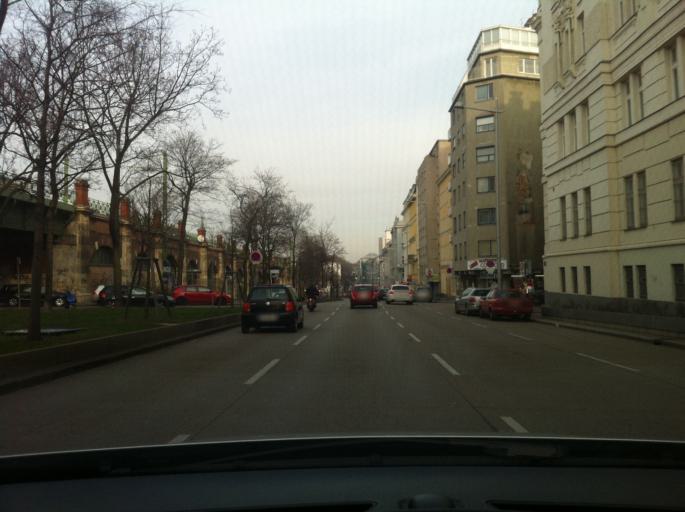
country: AT
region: Vienna
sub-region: Wien Stadt
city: Vienna
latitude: 48.2137
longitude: 16.3405
